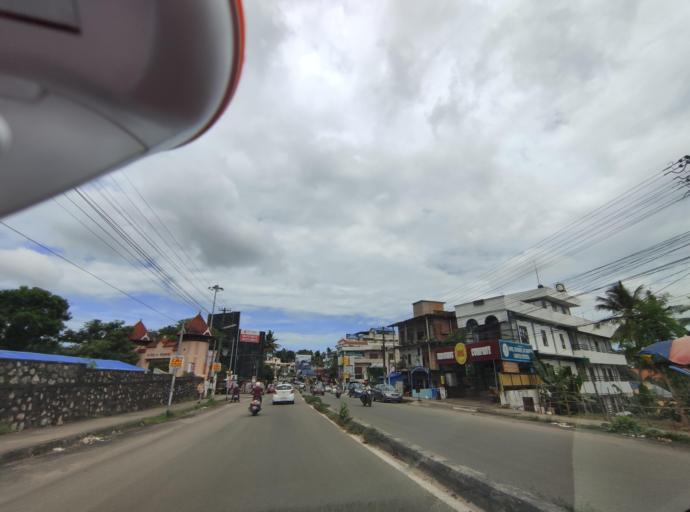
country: IN
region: Kerala
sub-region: Thiruvananthapuram
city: Thiruvananthapuram
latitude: 8.5322
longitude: 76.9402
